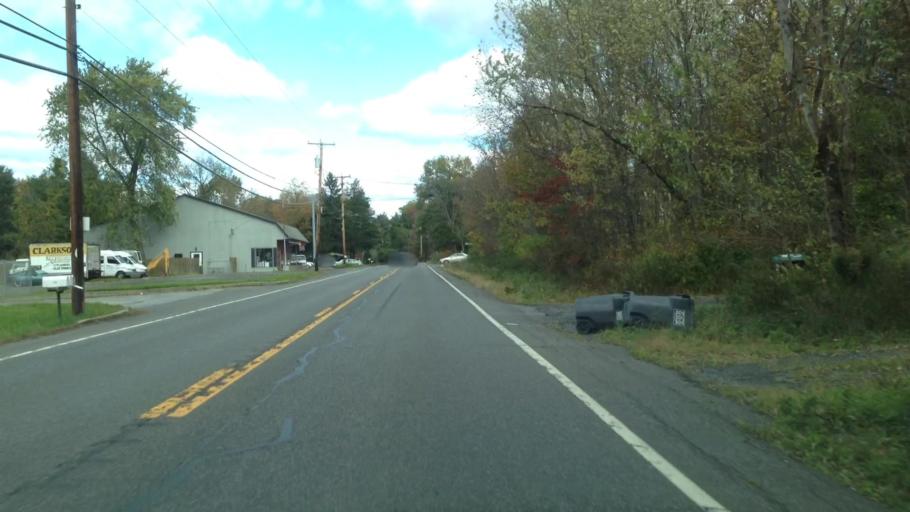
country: US
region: New York
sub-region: Ulster County
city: New Paltz
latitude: 41.7664
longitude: -74.0781
